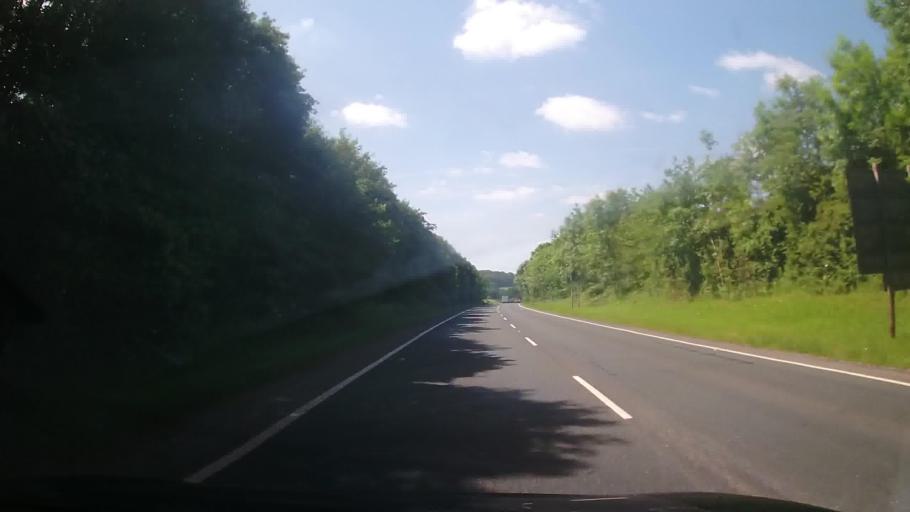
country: GB
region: England
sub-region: Shropshire
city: Ludlow
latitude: 52.3637
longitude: -2.6936
